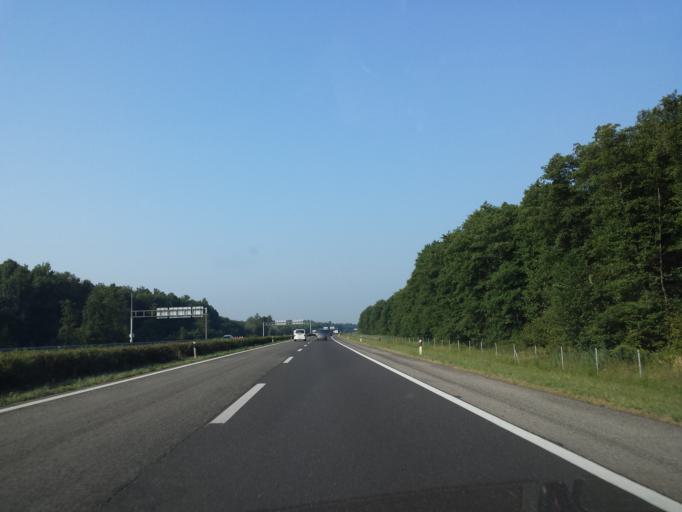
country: HR
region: Grad Zagreb
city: Brezovica
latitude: 45.7191
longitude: 15.8651
